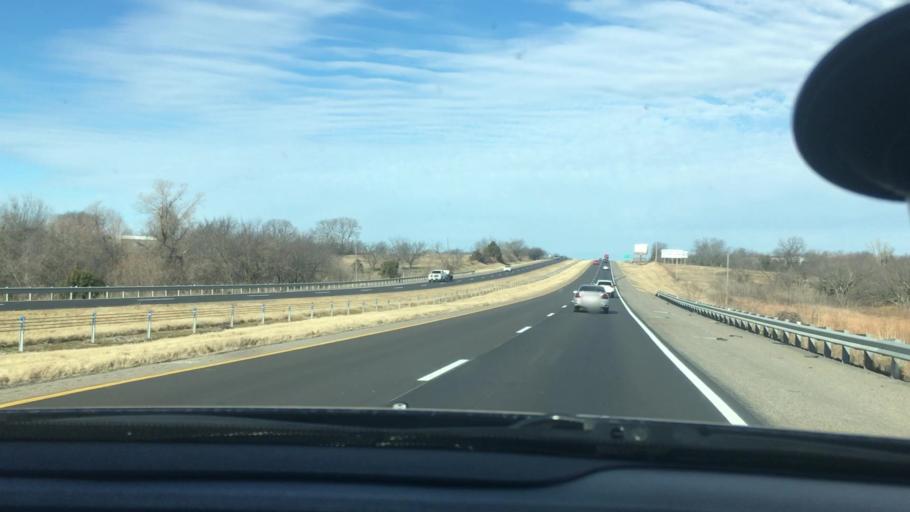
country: US
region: Oklahoma
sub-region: Cleveland County
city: Noble
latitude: 35.1027
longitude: -97.4299
